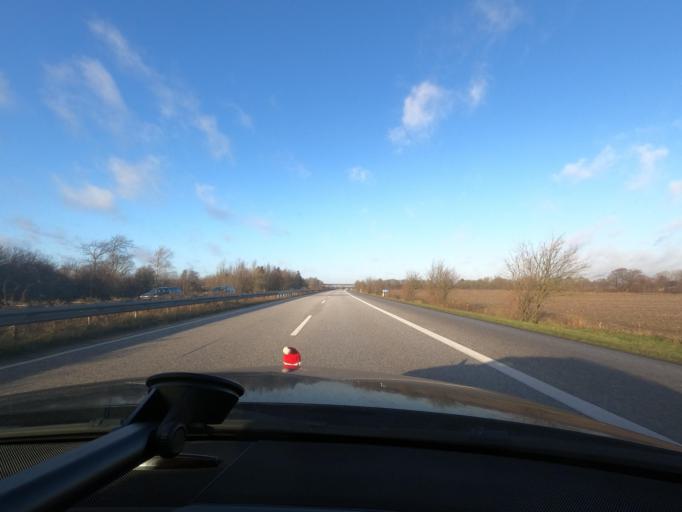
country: DE
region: Schleswig-Holstein
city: Sankelmark
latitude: 54.6992
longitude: 9.4046
